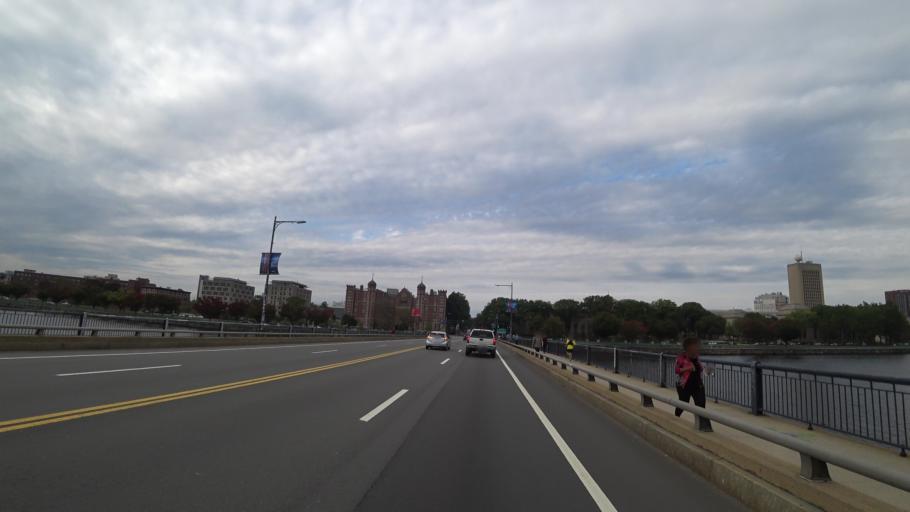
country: US
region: Massachusetts
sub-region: Middlesex County
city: Cambridge
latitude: 42.3558
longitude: -71.0918
